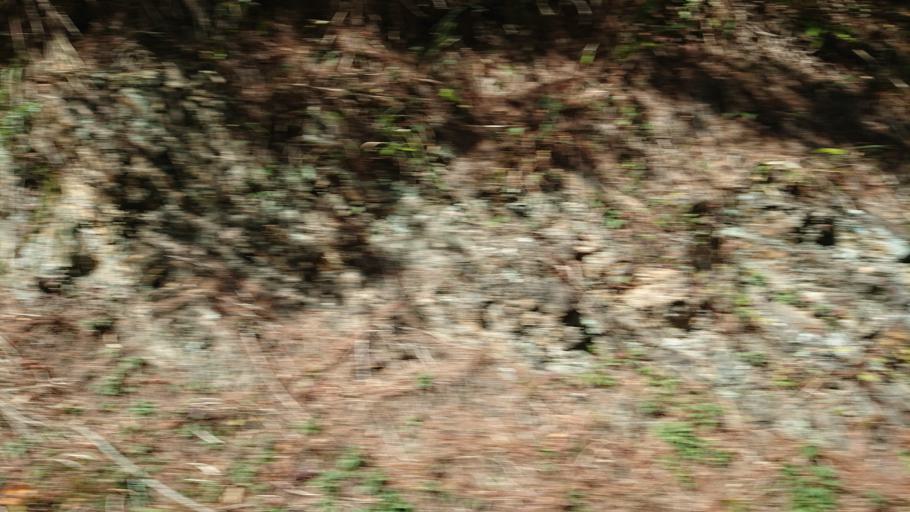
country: TW
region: Taiwan
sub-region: Hualien
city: Hualian
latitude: 24.3453
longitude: 121.3102
